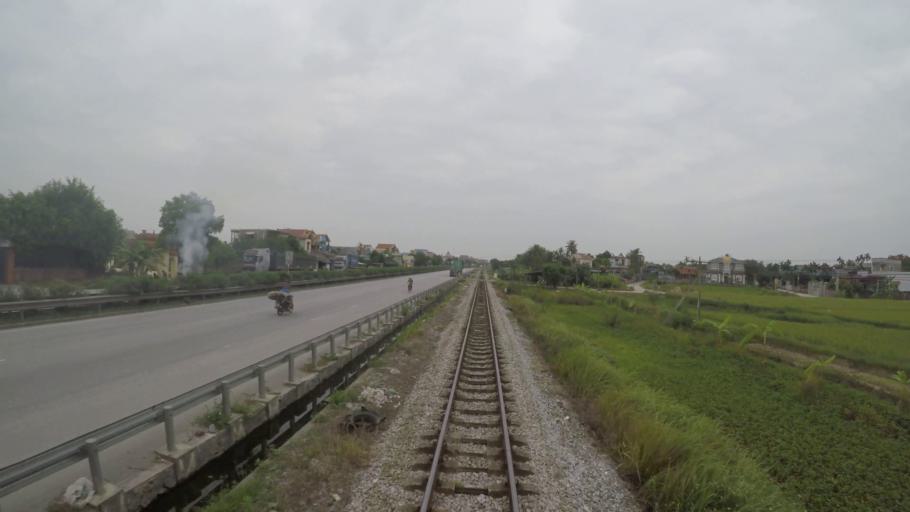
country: VN
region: Hai Duong
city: Phu Thai
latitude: 20.9601
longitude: 106.5217
